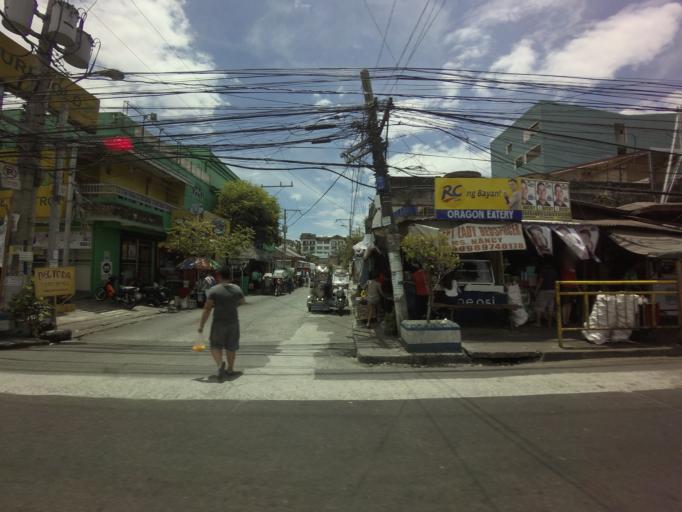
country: PH
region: Calabarzon
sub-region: Province of Rizal
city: Cainta
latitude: 14.5890
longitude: 121.0973
